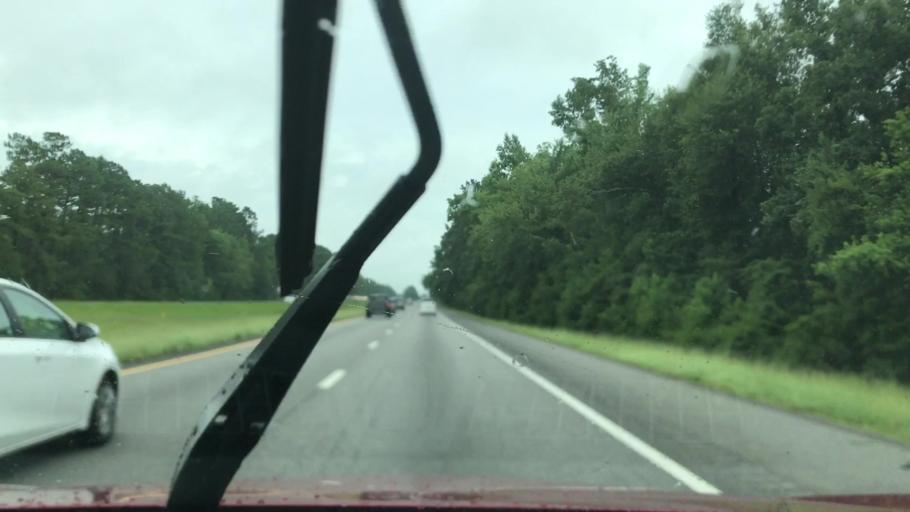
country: US
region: South Carolina
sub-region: Dorchester County
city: Ridgeville
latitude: 33.1829
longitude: -80.3809
